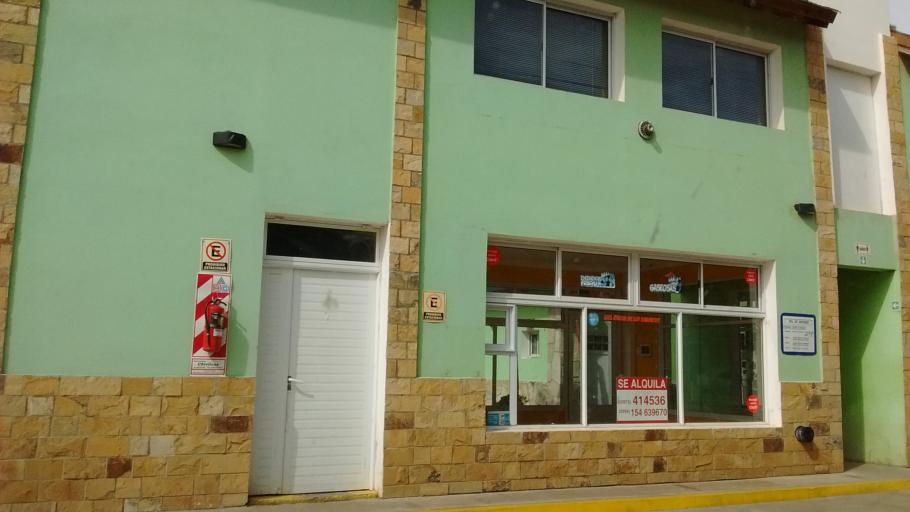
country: AR
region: Neuquen
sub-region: Departamento de Lacar
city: San Martin de los Andes
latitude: -40.1268
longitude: -71.2529
